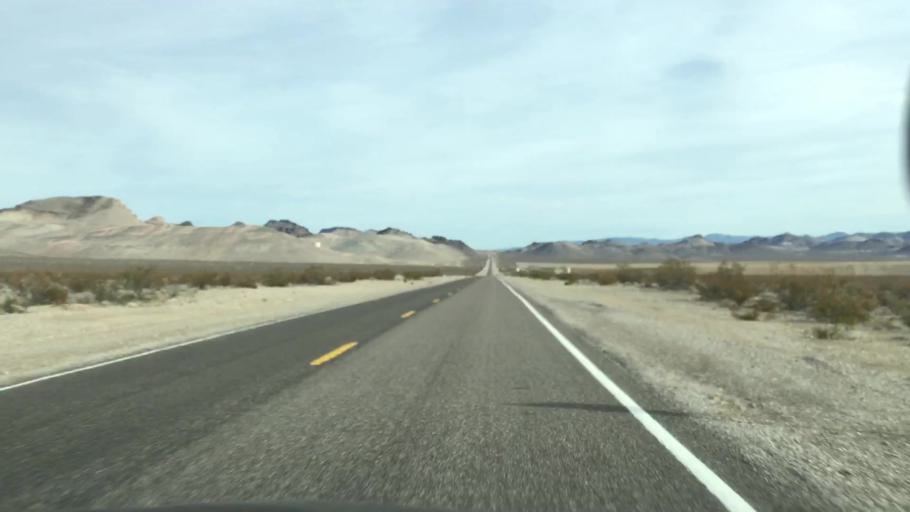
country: US
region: Nevada
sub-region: Nye County
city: Beatty
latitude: 36.8730
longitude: -116.8271
